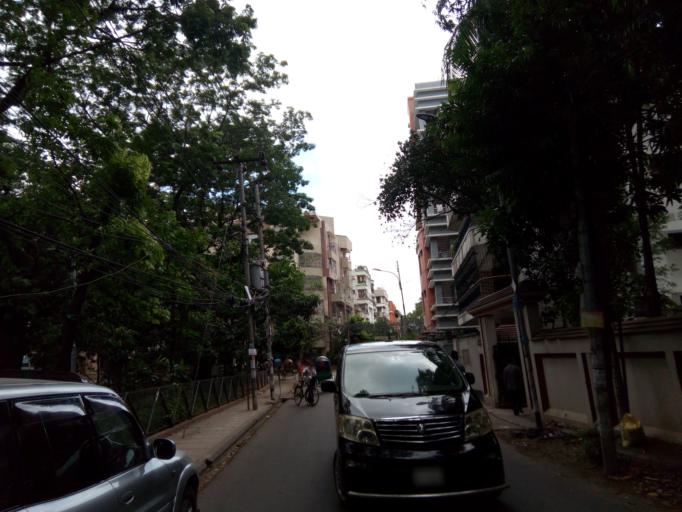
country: BD
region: Dhaka
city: Azimpur
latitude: 23.7469
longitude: 90.3774
